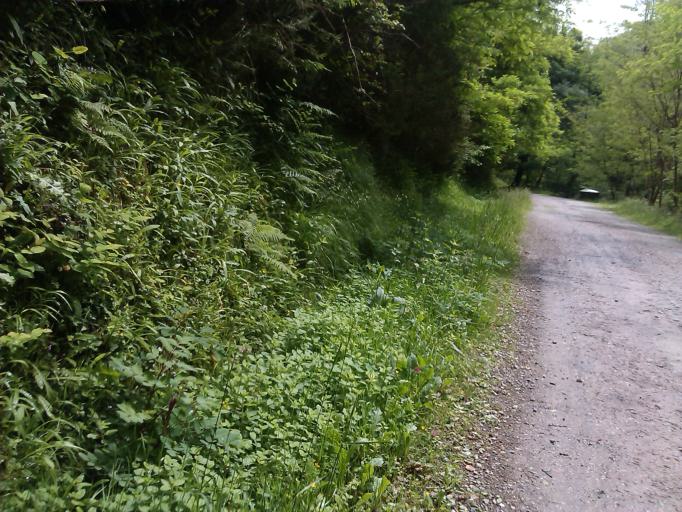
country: ES
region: Basque Country
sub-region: Provincia de Guipuzcoa
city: Andoain
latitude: 43.1871
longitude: -2.0029
